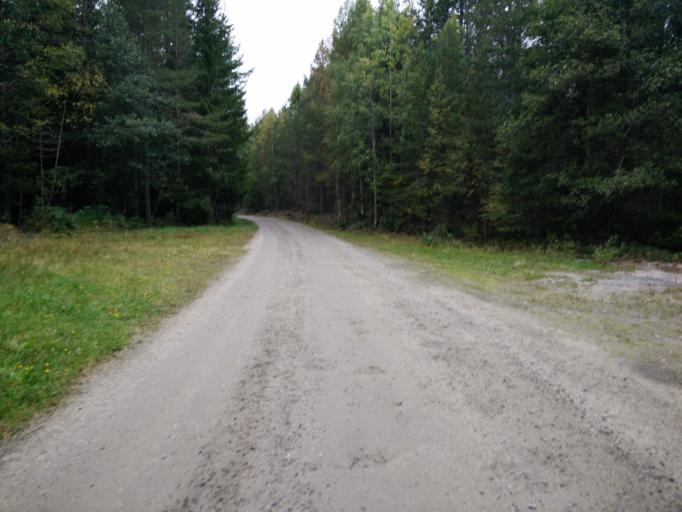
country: SE
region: Gaevleborg
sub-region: Hudiksvalls Kommun
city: Hudiksvall
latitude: 61.8329
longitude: 17.3342
